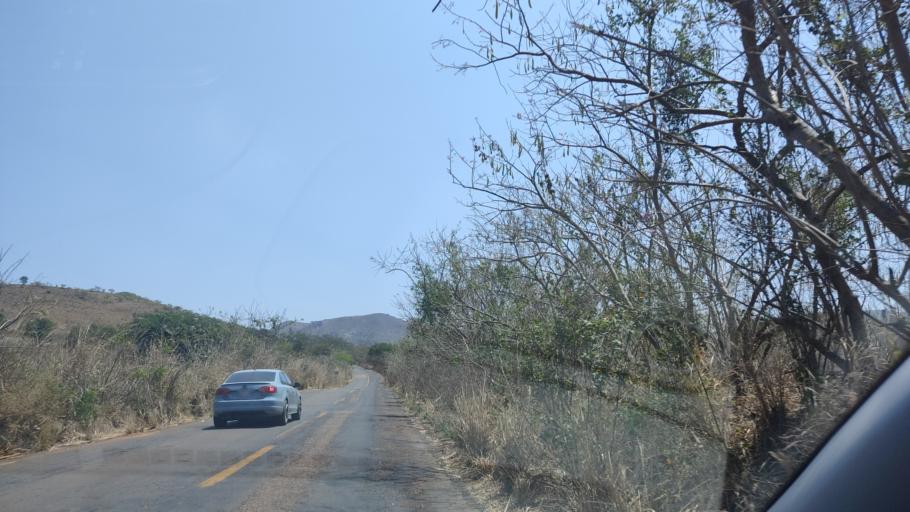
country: MX
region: Nayarit
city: Puga
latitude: 21.5785
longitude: -104.7681
